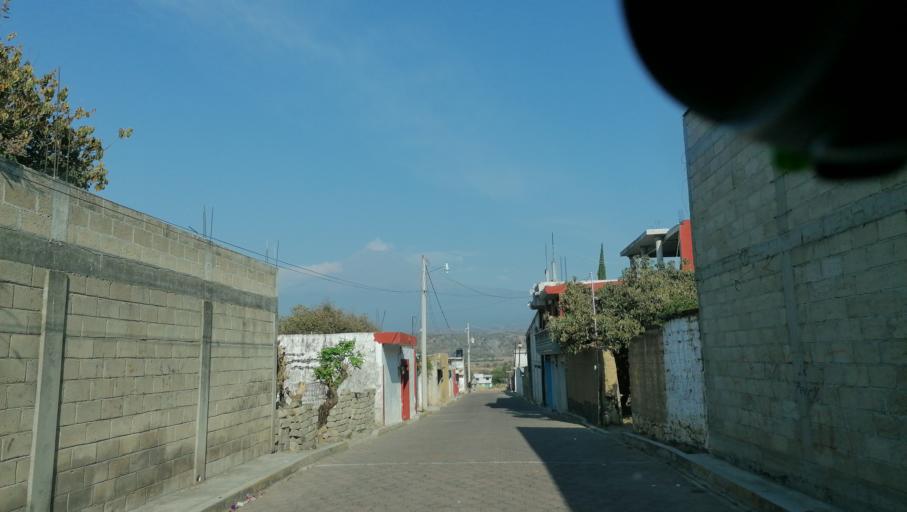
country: MX
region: Puebla
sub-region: Tianguismanalco
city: San Martin Tlapala
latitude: 18.9729
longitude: -98.4499
